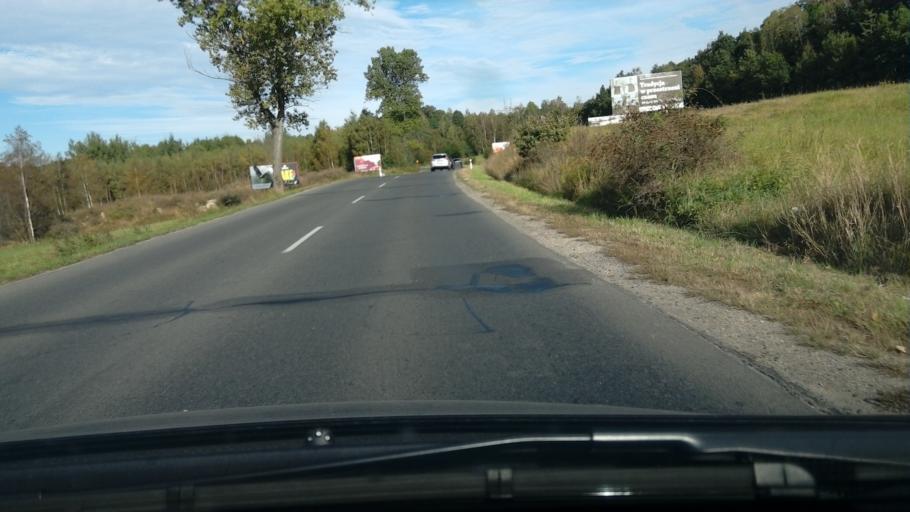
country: PL
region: Lower Silesian Voivodeship
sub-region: Powiat jeleniogorski
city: Myslakowice
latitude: 50.8638
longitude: 15.7733
